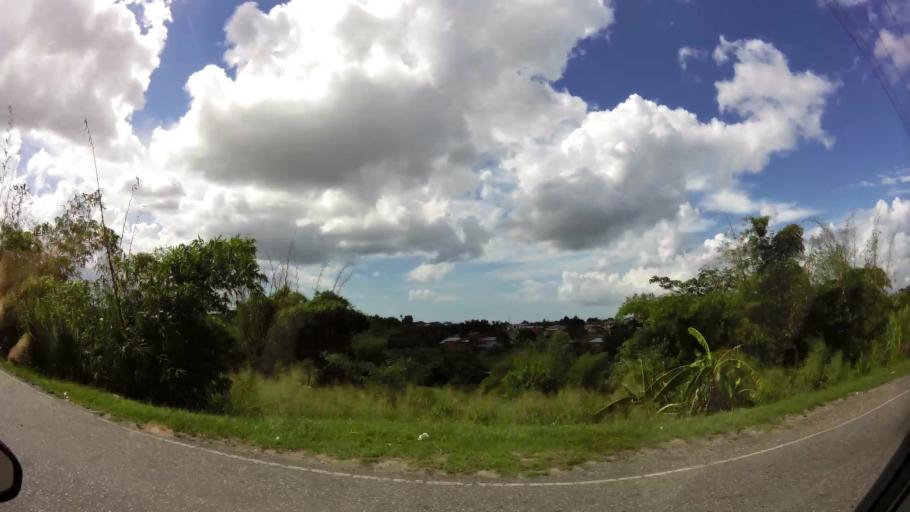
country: TT
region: Penal/Debe
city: Debe
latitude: 10.2399
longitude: -61.4407
